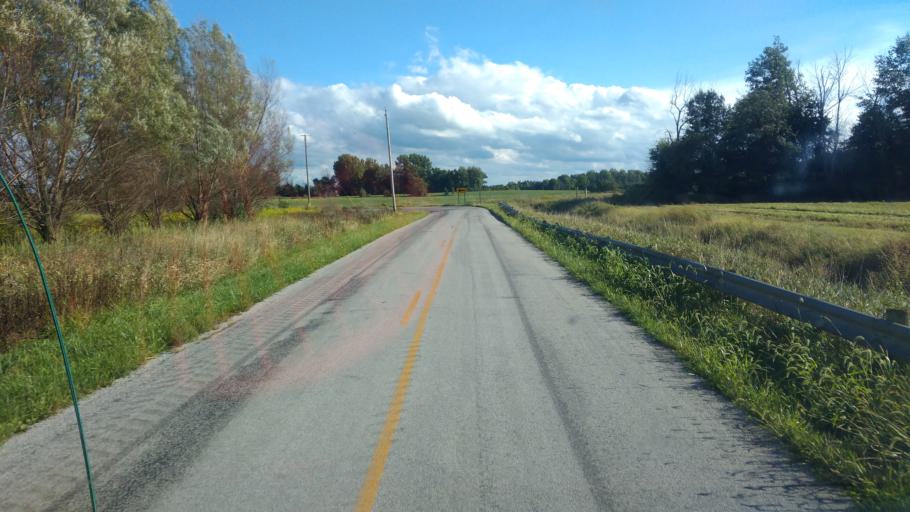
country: US
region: Ohio
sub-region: Hardin County
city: Forest
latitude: 40.7539
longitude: -83.6048
